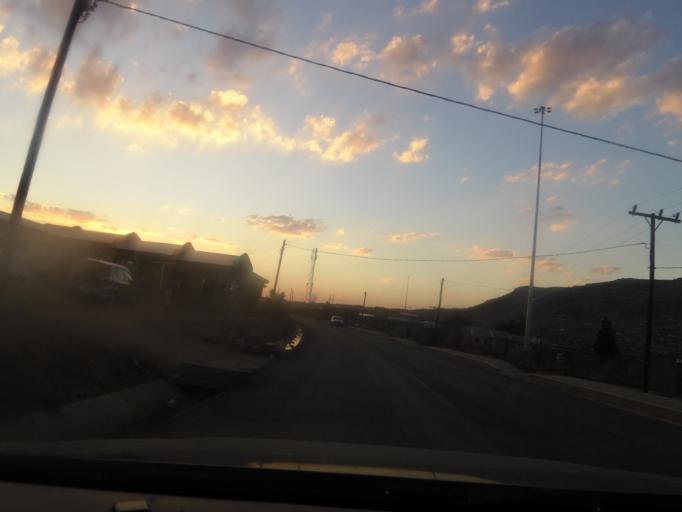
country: LS
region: Maseru
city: Maseru
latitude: -29.3661
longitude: 27.4751
